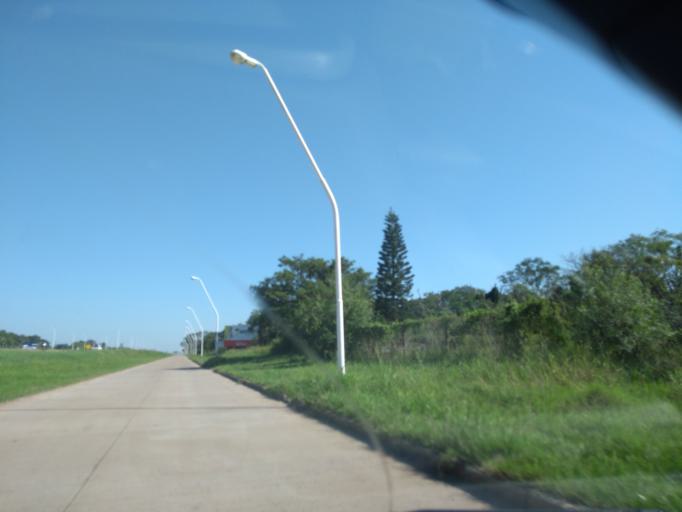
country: AR
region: Chaco
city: Barranqueras
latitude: -27.4346
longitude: -58.9220
